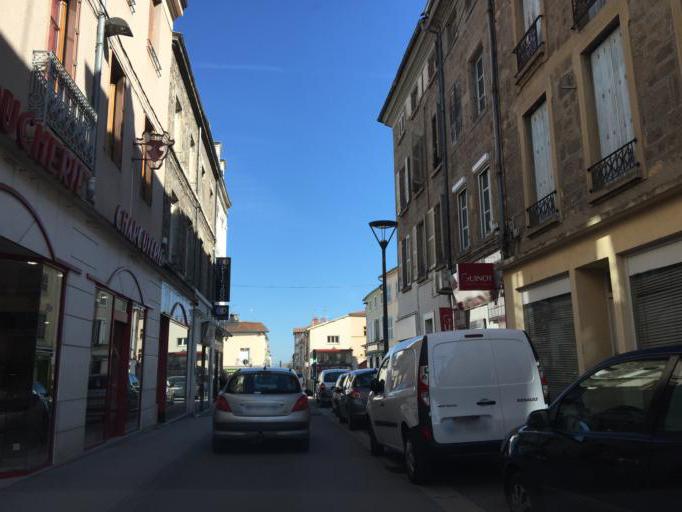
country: FR
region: Rhone-Alpes
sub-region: Departement de la Loire
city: Feurs
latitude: 45.7430
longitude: 4.2233
